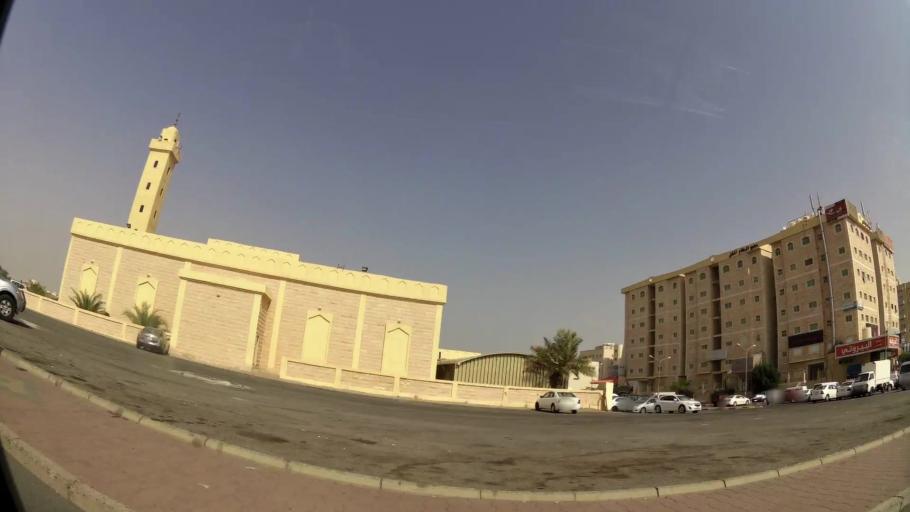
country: KW
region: Muhafazat al Jahra'
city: Al Jahra'
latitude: 29.3426
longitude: 47.6668
